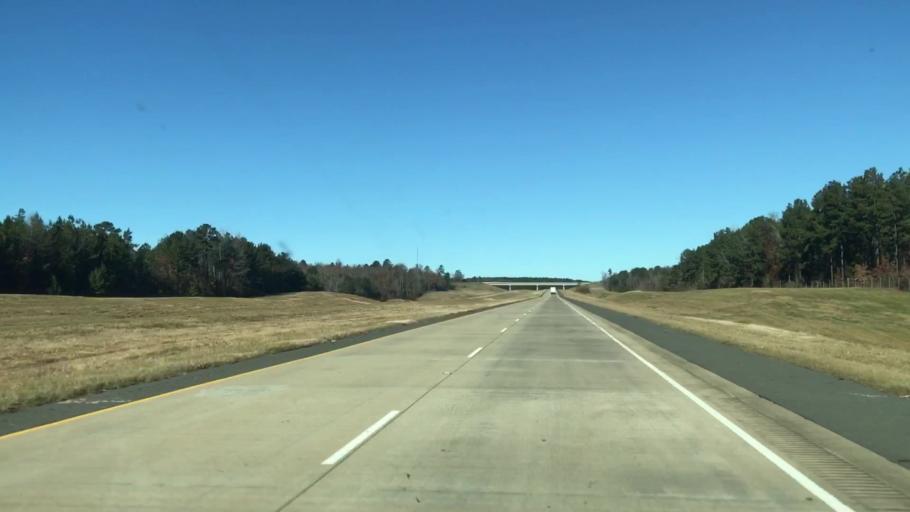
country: US
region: Louisiana
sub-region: Caddo Parish
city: Vivian
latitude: 32.9167
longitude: -93.8787
